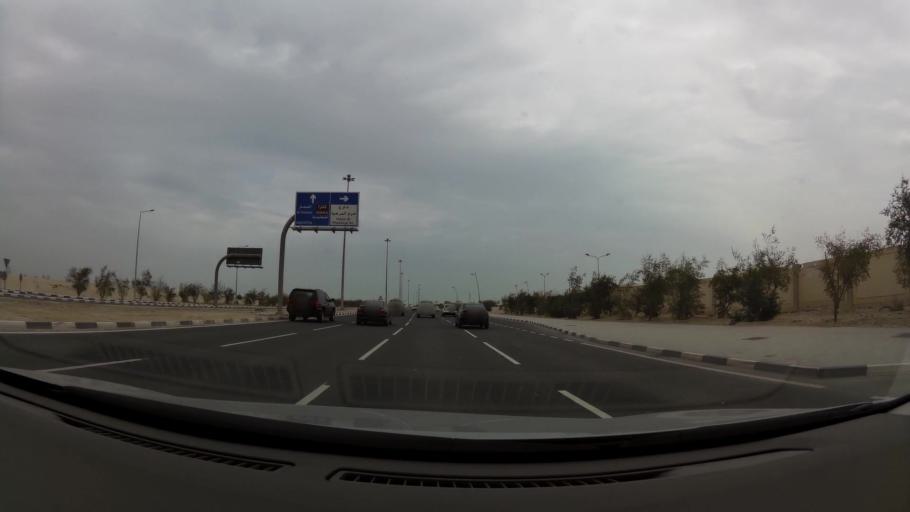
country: QA
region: Baladiyat ad Dawhah
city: Doha
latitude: 25.3487
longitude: 51.4840
